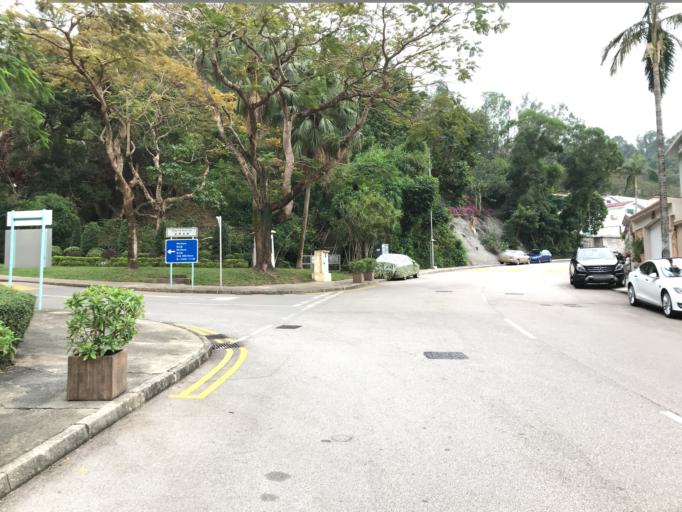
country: HK
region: Tai Po
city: Tai Po
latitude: 22.4613
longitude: 114.1560
